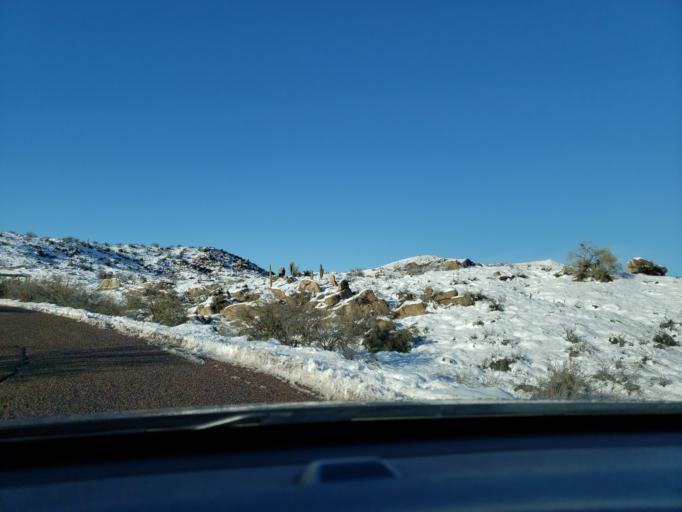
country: US
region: Arizona
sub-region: Maricopa County
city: Carefree
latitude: 33.8848
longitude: -111.8156
